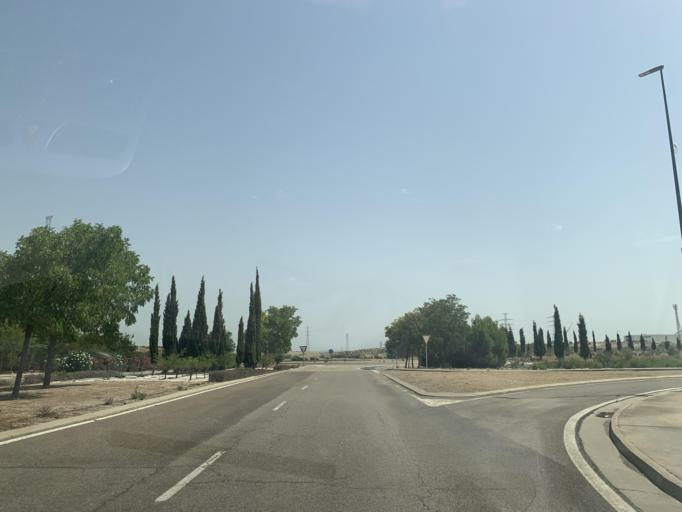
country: ES
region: Aragon
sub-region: Provincia de Zaragoza
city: Zaragoza
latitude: 41.5891
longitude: -0.8324
